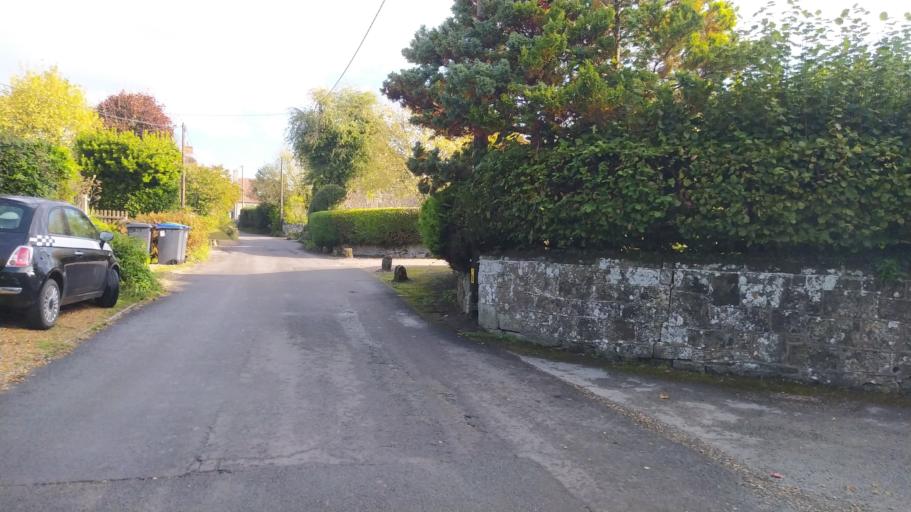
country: GB
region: England
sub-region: Dorset
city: Shaftesbury
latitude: 51.0140
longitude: -2.1304
